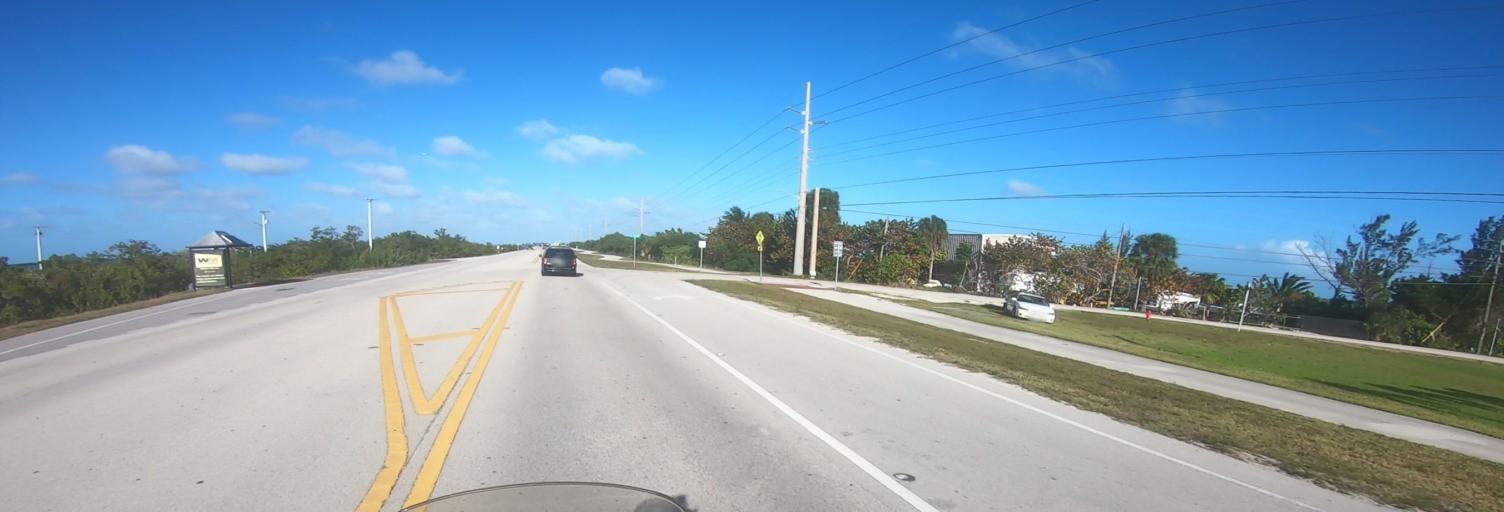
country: US
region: Florida
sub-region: Monroe County
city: Big Coppitt Key
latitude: 24.6292
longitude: -81.5926
